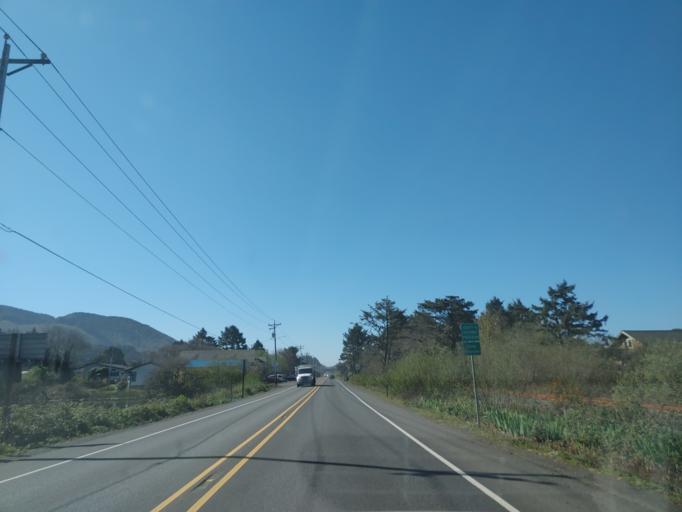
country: US
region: Oregon
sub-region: Tillamook County
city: Rockaway Beach
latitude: 45.5999
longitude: -123.9462
